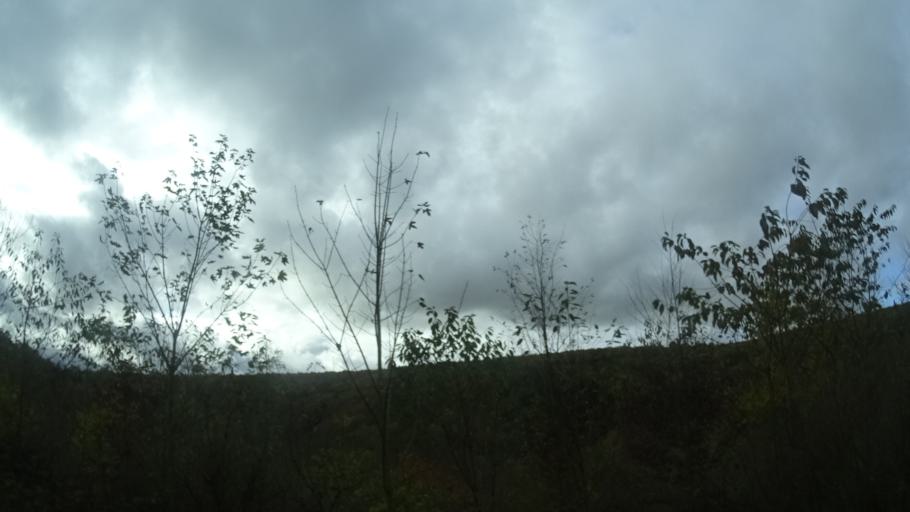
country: DE
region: Bavaria
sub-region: Regierungsbezirk Unterfranken
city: Aubstadt
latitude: 50.3533
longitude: 10.4188
